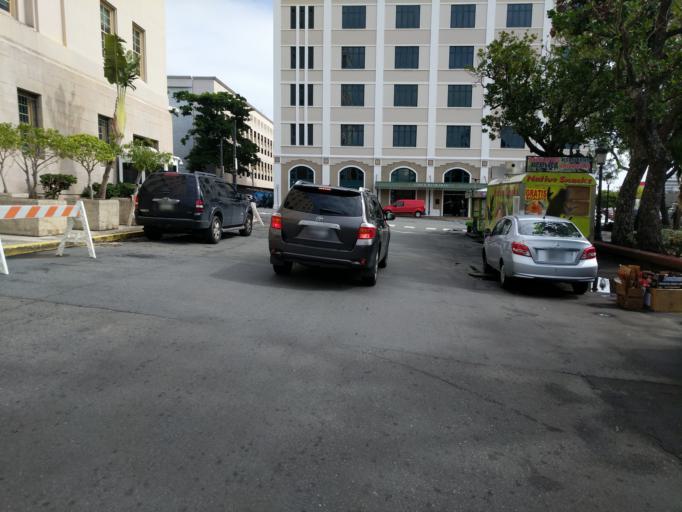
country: PR
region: San Juan
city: San Juan
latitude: 18.4635
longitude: -66.1146
